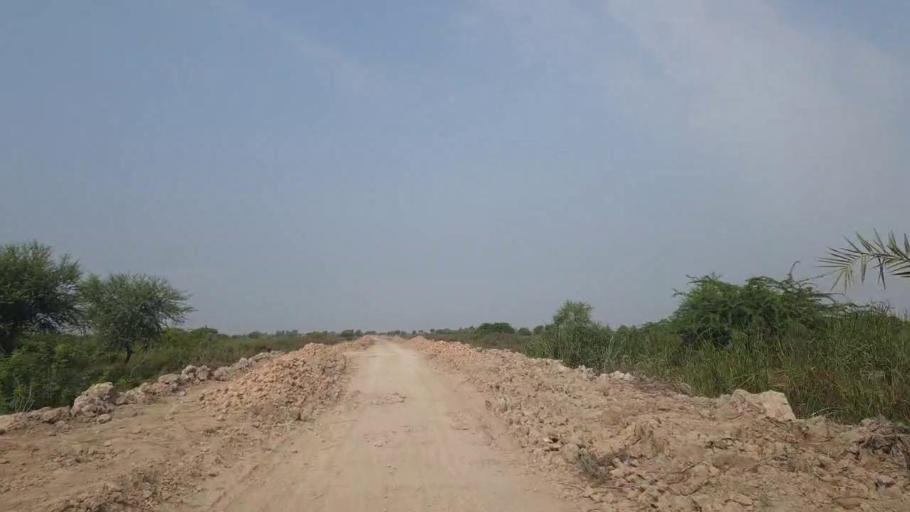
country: PK
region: Sindh
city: Badin
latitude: 24.6072
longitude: 68.7416
